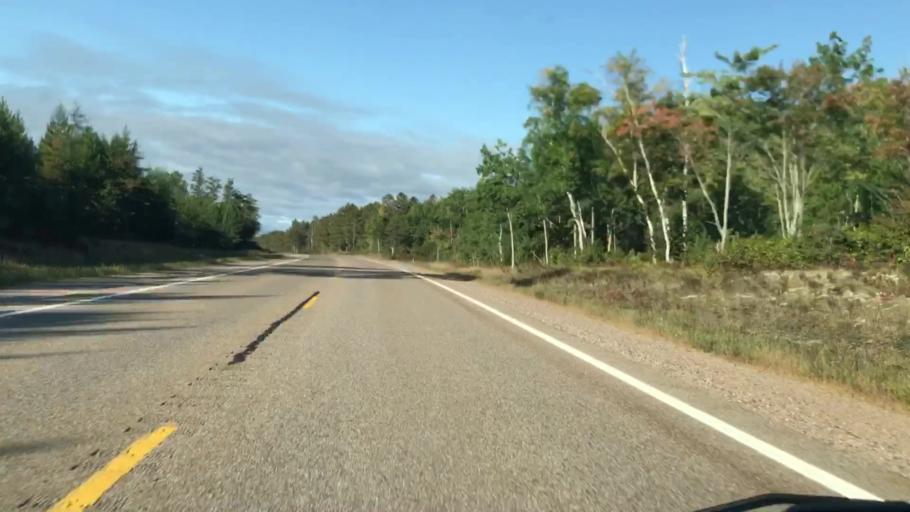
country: US
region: Michigan
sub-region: Mackinac County
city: Saint Ignace
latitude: 46.3572
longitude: -84.8912
